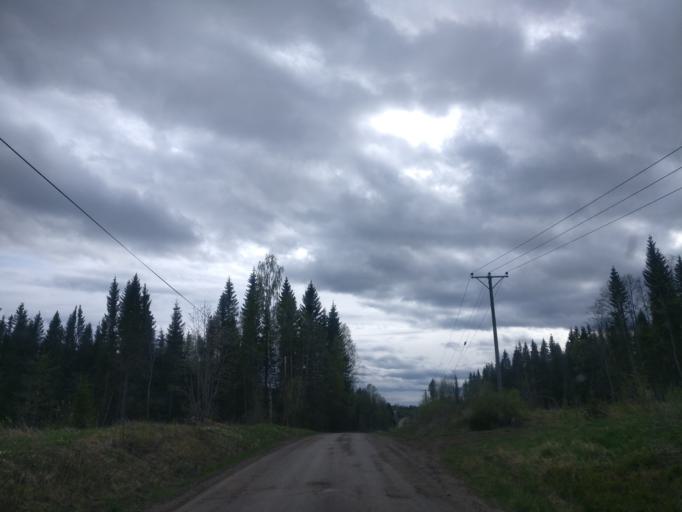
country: SE
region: Vaesternorrland
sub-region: Timra Kommun
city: Soraker
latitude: 62.5184
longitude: 17.5737
